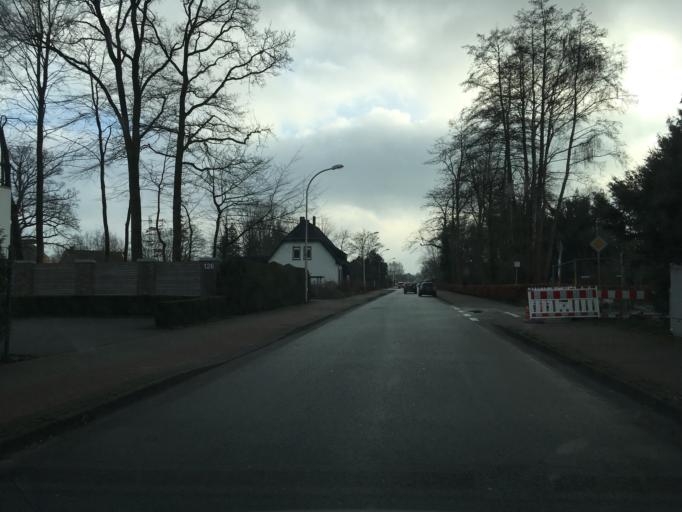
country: DE
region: North Rhine-Westphalia
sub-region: Regierungsbezirk Munster
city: Gronau
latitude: 52.2249
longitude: 7.0101
